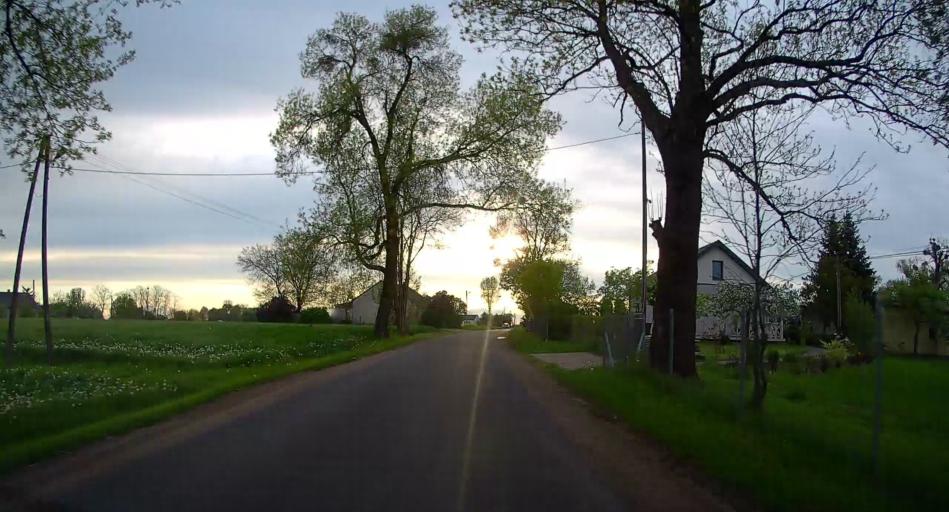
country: PL
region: Masovian Voivodeship
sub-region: Powiat plocki
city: Mala Wies
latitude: 52.4546
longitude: 20.0932
